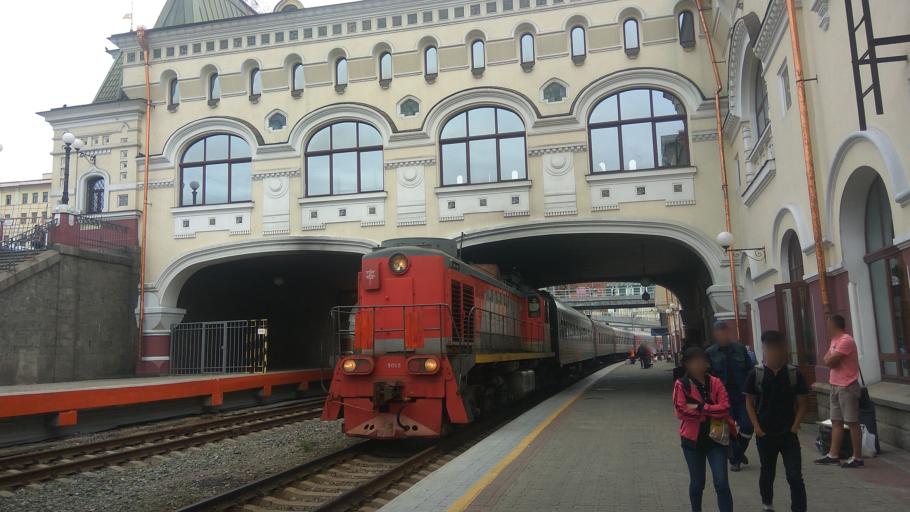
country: RU
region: Primorskiy
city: Vladivostok
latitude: 43.1109
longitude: 131.8814
